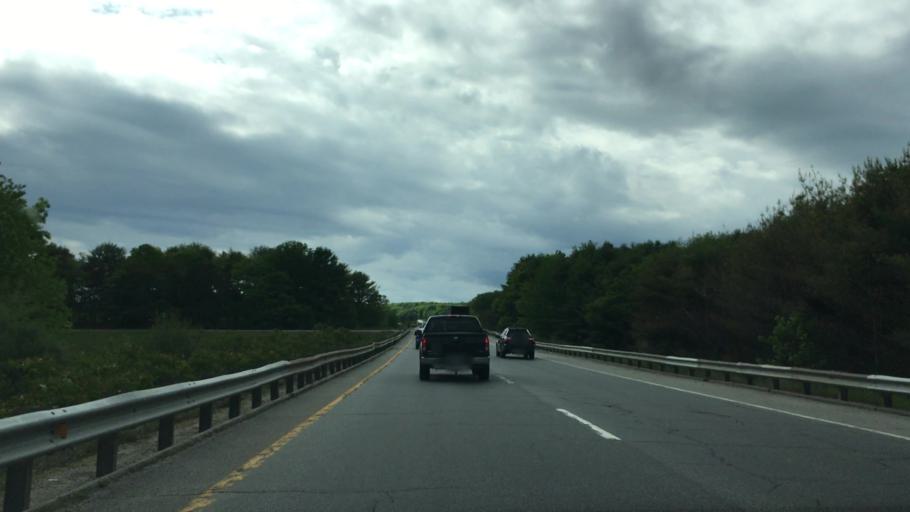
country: US
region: Maine
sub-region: Sagadahoc County
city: Bath
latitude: 43.9155
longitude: -69.8531
